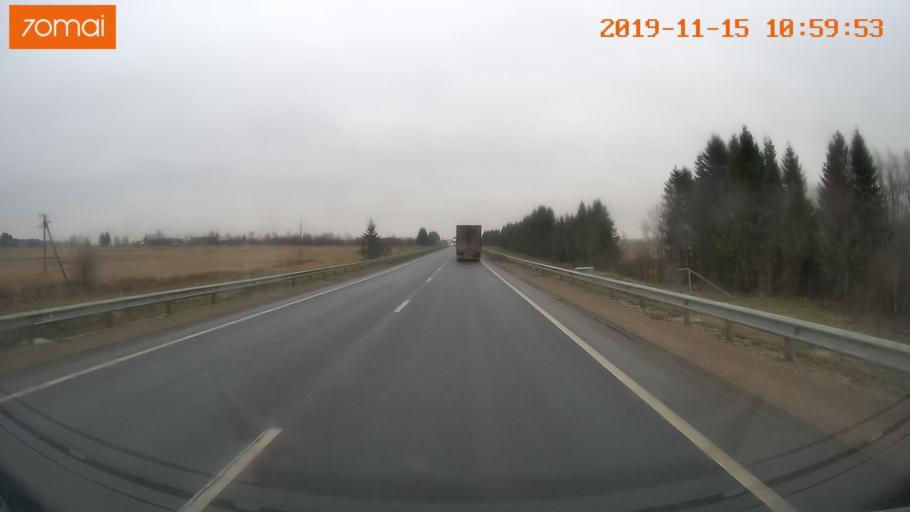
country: RU
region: Vologda
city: Chebsara
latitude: 59.1397
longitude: 38.8874
